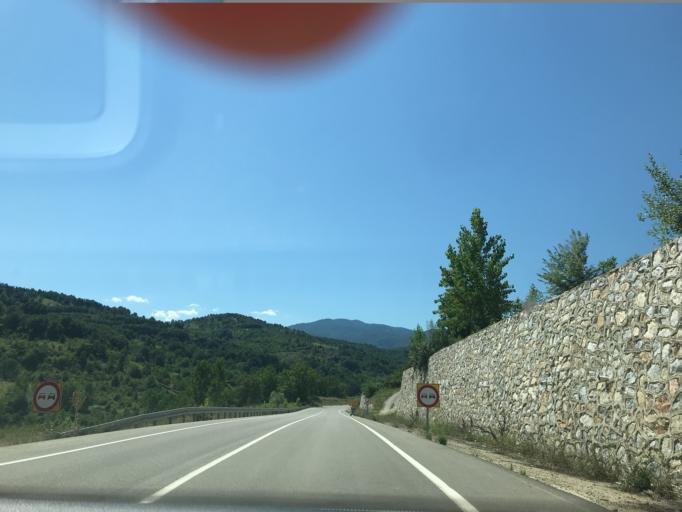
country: TR
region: Bursa
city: Tahtakopru
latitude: 39.9748
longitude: 29.6048
